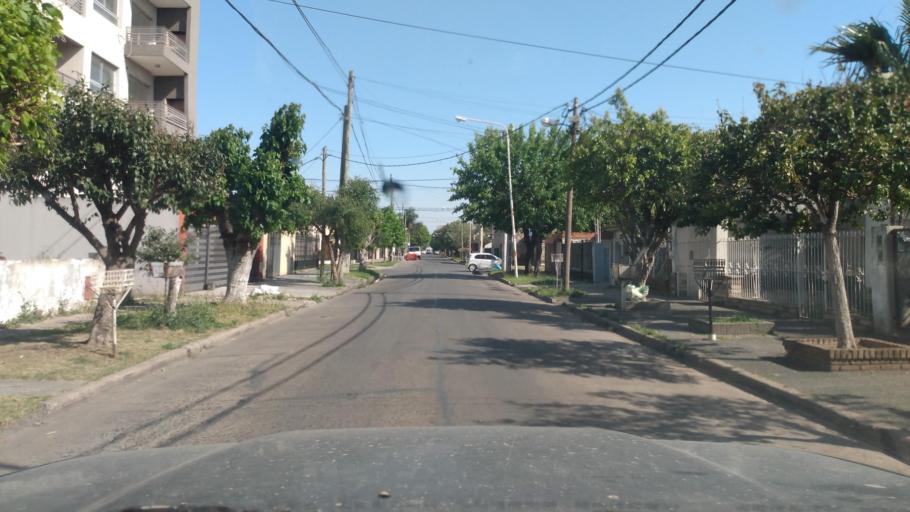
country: AR
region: Buenos Aires
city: San Justo
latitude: -34.6680
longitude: -58.5779
